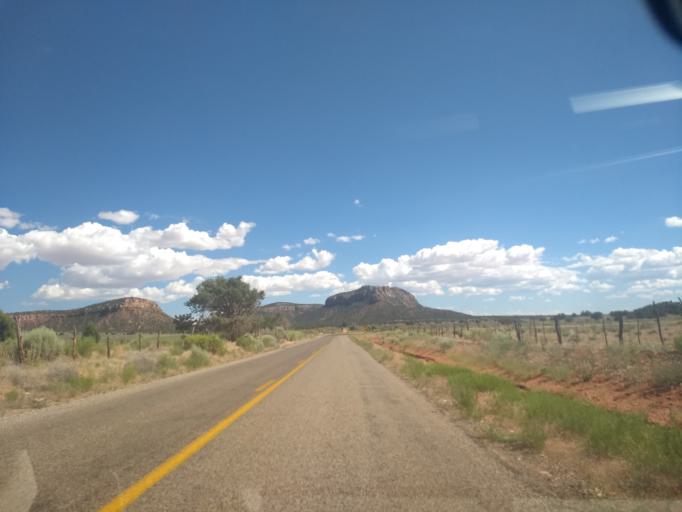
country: US
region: Utah
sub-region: Washington County
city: Hildale
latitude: 36.9487
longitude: -112.8746
